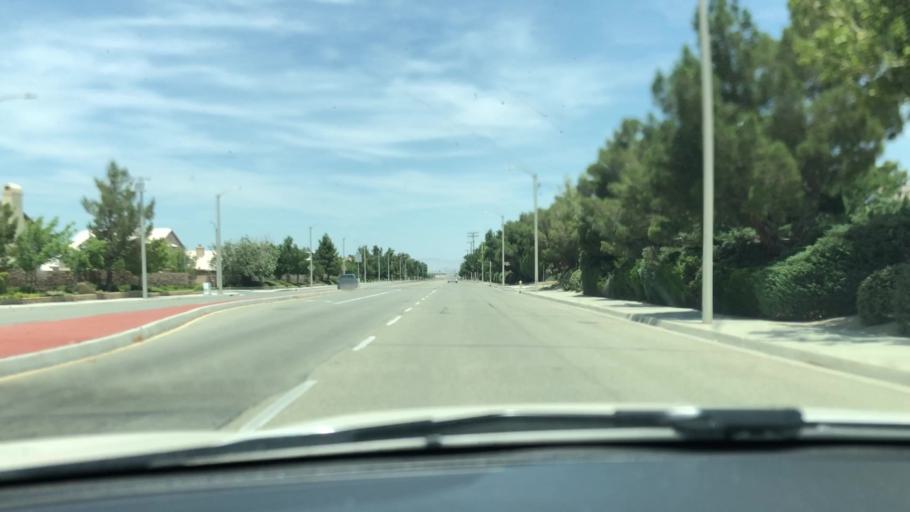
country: US
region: California
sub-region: Los Angeles County
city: Quartz Hill
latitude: 34.6833
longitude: -118.2014
